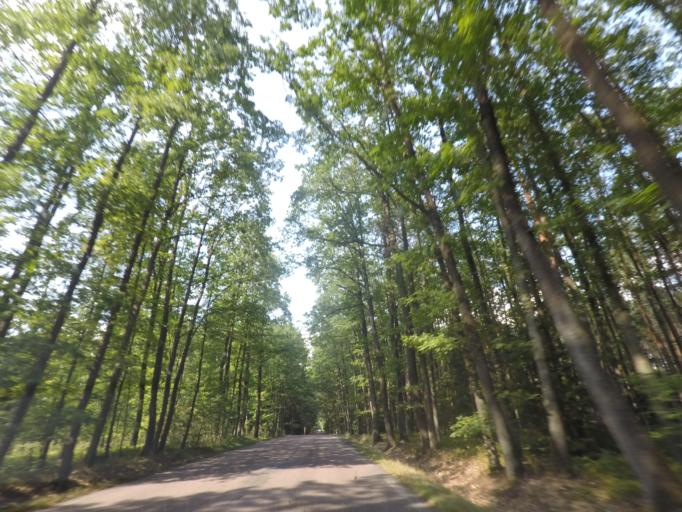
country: CZ
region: Pardubicky
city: Horni Jeleni
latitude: 50.0204
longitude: 16.0814
